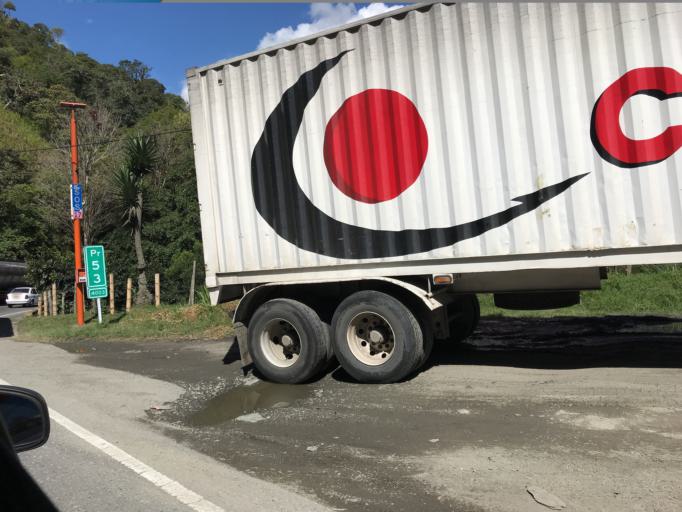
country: CO
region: Tolima
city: Cajamarca
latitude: 4.4377
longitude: -75.4017
